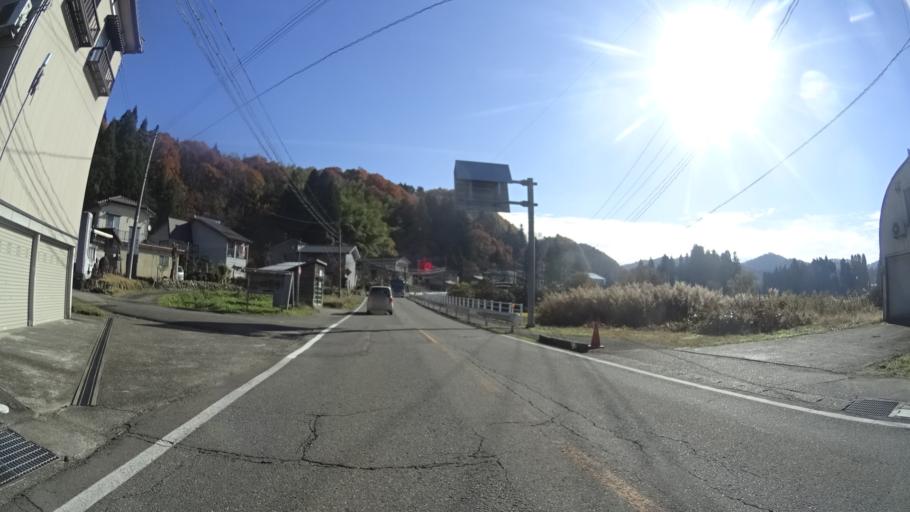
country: JP
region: Niigata
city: Tochio-honcho
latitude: 37.4891
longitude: 138.9758
